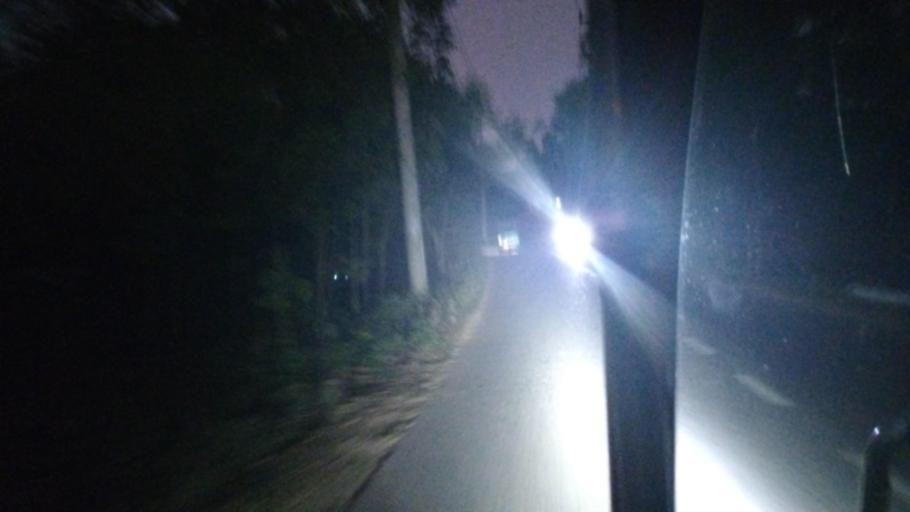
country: BD
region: Dhaka
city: Sakhipur
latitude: 24.4011
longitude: 90.3517
